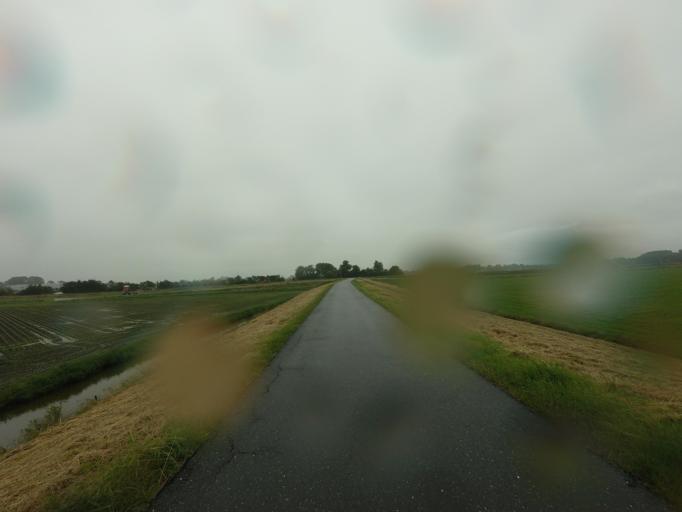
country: NL
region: North Holland
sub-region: Gemeente Schagen
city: Schagen
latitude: 52.8013
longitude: 4.7801
